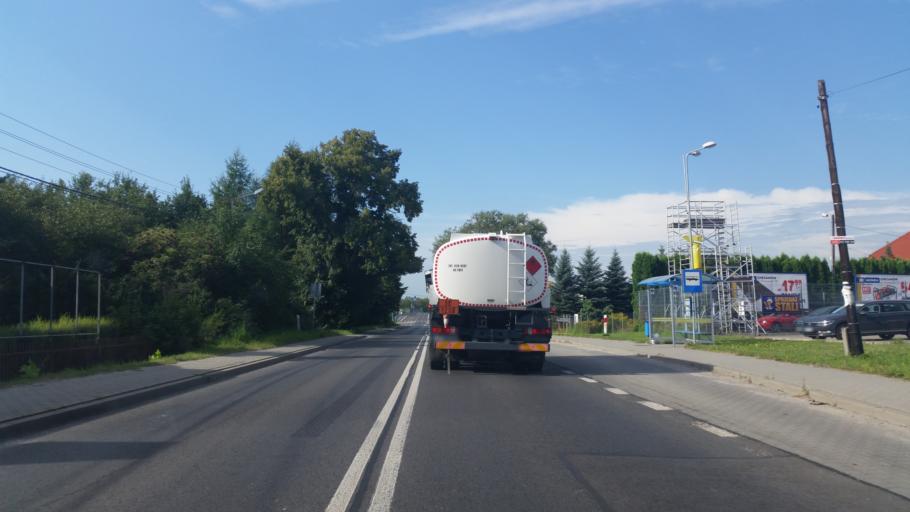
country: PL
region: Lesser Poland Voivodeship
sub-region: Powiat chrzanowski
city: Chrzanow
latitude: 50.1265
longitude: 19.3679
